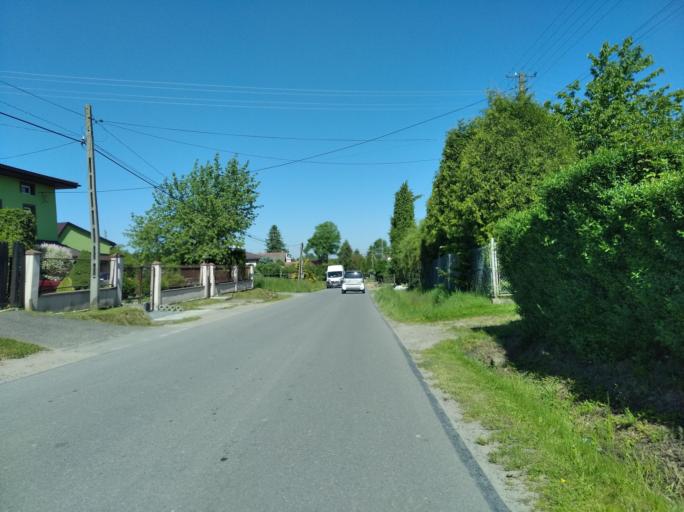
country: PL
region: Subcarpathian Voivodeship
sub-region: Powiat krosnienski
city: Korczyna
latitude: 49.7186
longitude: 21.7942
